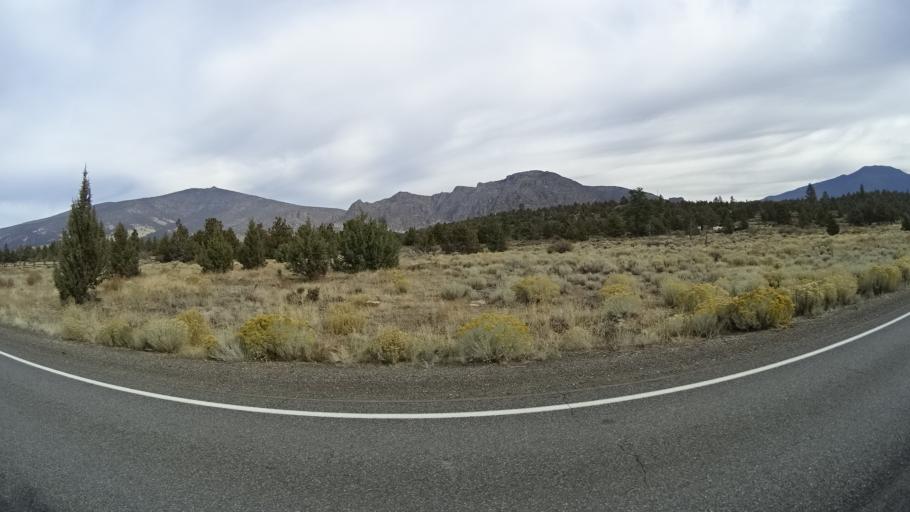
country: US
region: California
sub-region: Siskiyou County
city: Weed
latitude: 41.5663
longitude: -122.2655
